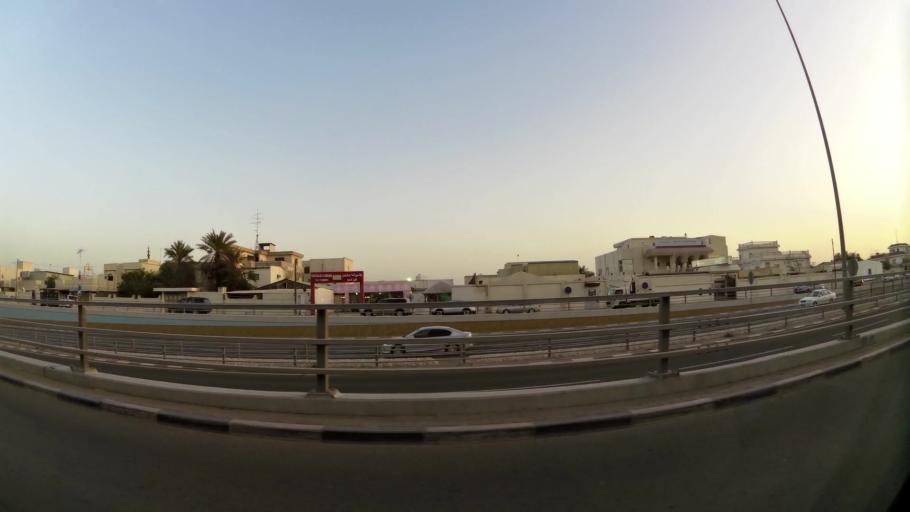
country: QA
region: Baladiyat ar Rayyan
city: Ar Rayyan
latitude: 25.3205
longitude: 51.4669
